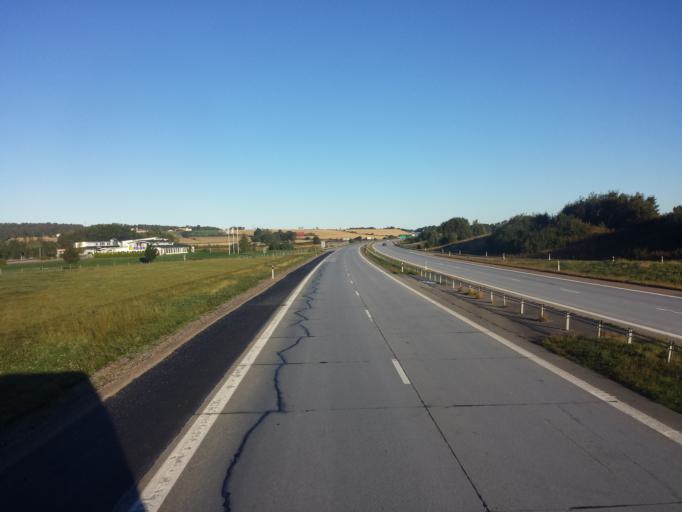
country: SE
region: Halland
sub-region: Falkenbergs Kommun
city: Falkenberg
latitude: 56.8849
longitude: 12.6060
